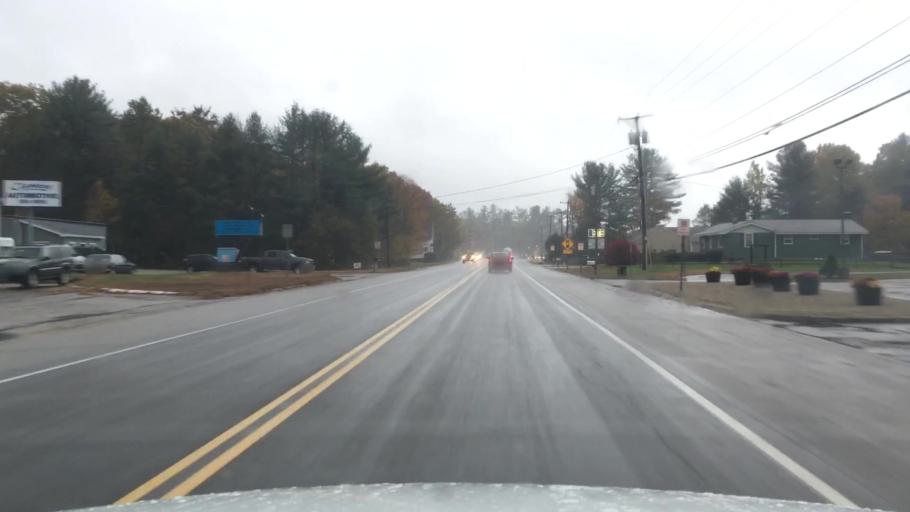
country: US
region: New Hampshire
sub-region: Strafford County
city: Rochester
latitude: 43.2575
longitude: -70.9791
